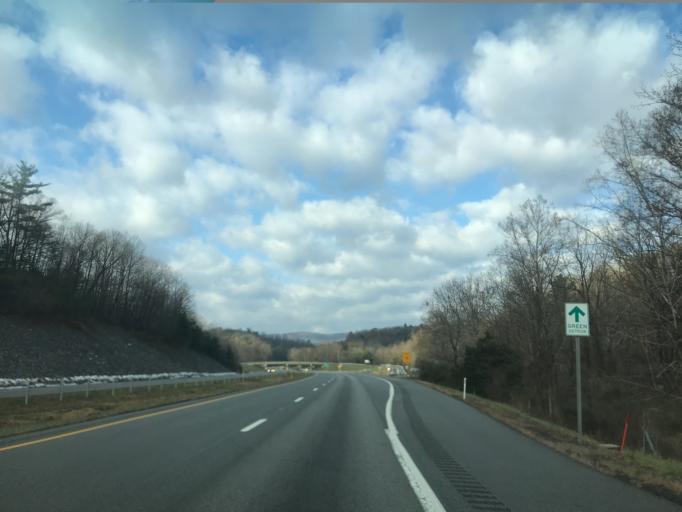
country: US
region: Maryland
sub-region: Washington County
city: Hancock
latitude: 39.7981
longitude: -78.2402
